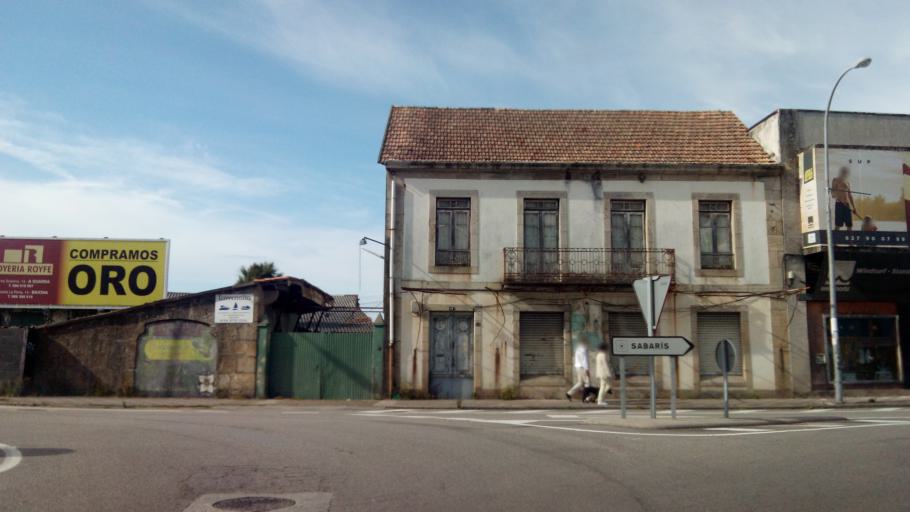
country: ES
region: Galicia
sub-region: Provincia de Pontevedra
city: Baiona
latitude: 42.1113
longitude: -8.8351
